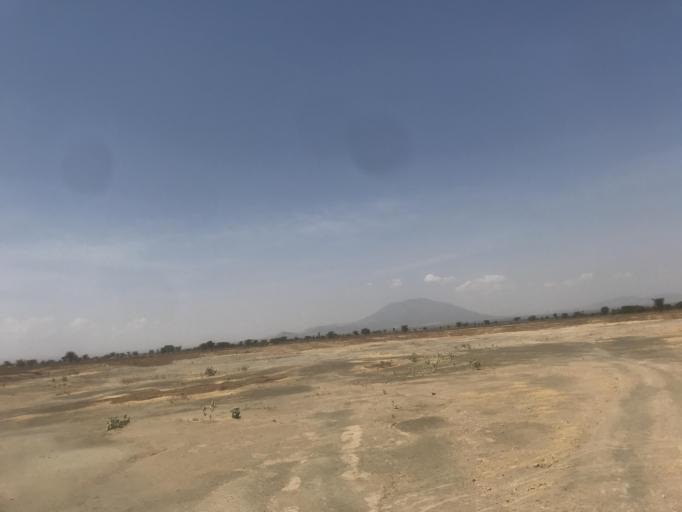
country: ET
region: Oromiya
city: Mojo
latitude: 8.3151
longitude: 38.9476
